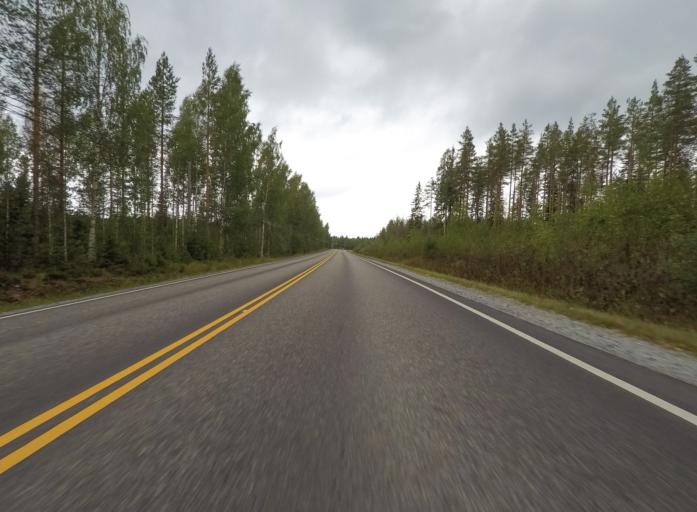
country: FI
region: Central Finland
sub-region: Jyvaeskylae
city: Hankasalmi
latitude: 62.3525
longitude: 26.4584
